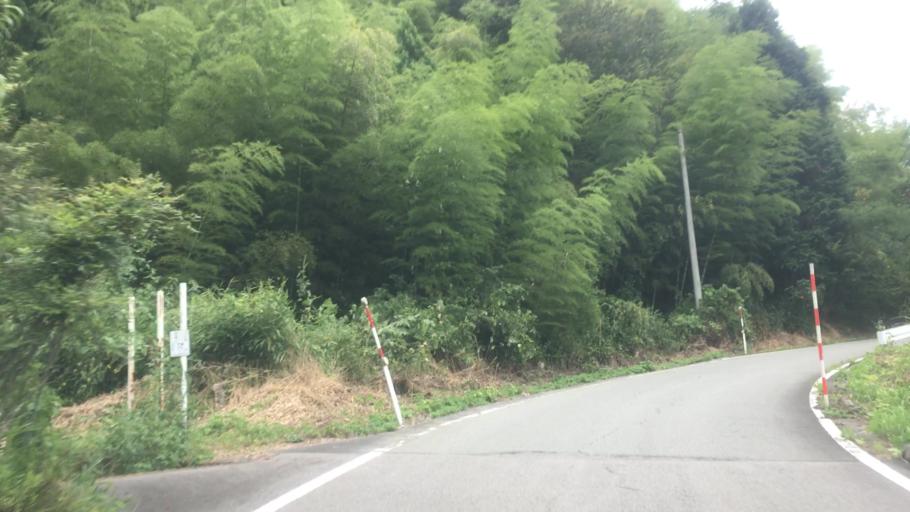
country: JP
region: Hyogo
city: Toyooka
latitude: 35.5978
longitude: 134.8007
